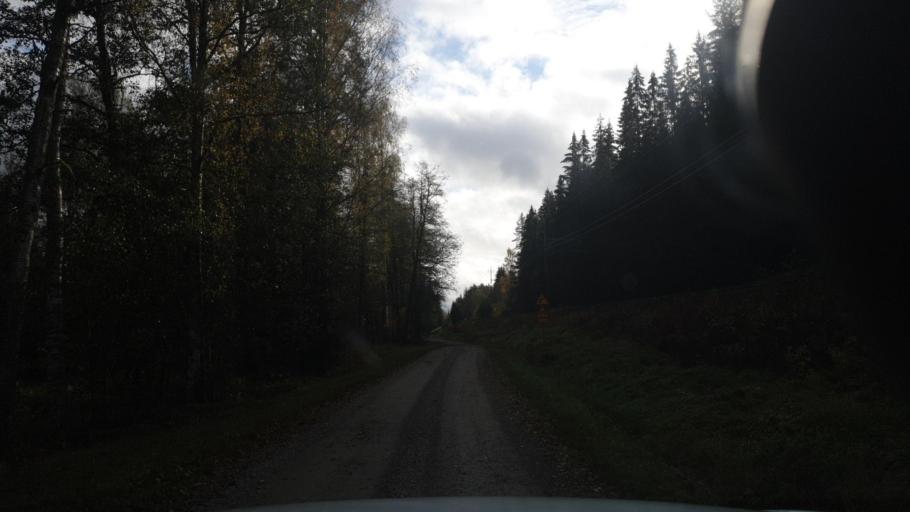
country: SE
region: Vaermland
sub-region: Karlstads Kommun
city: Edsvalla
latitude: 59.6126
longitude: 12.9791
